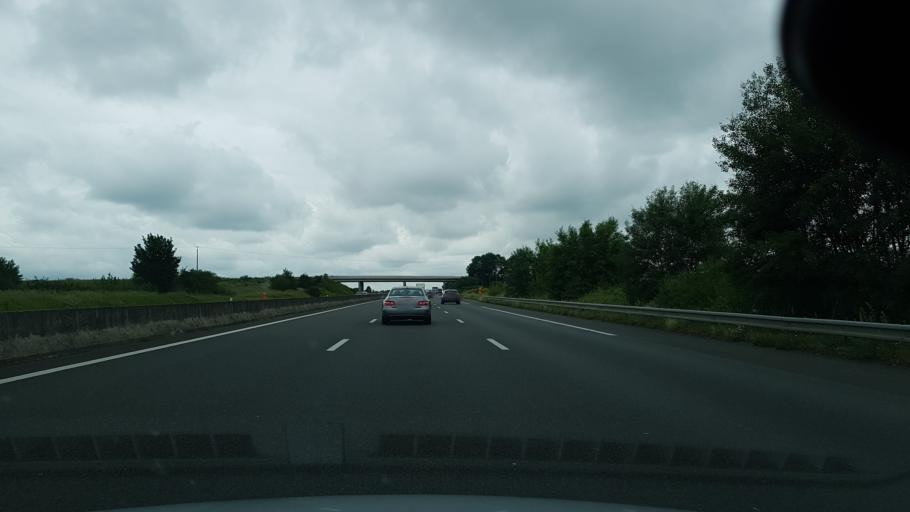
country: FR
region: Centre
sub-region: Departement du Loir-et-Cher
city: Herbault
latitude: 47.5903
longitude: 1.0871
